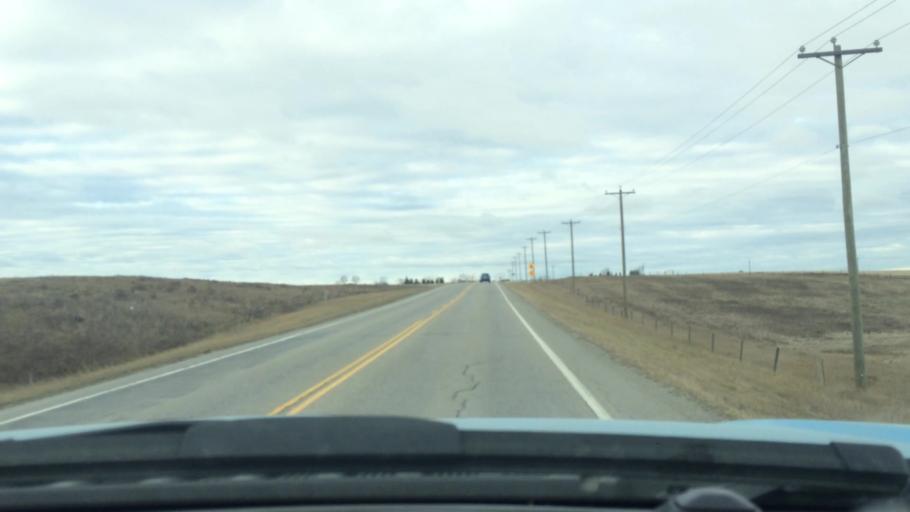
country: CA
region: Alberta
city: Airdrie
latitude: 51.2126
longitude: -114.0192
